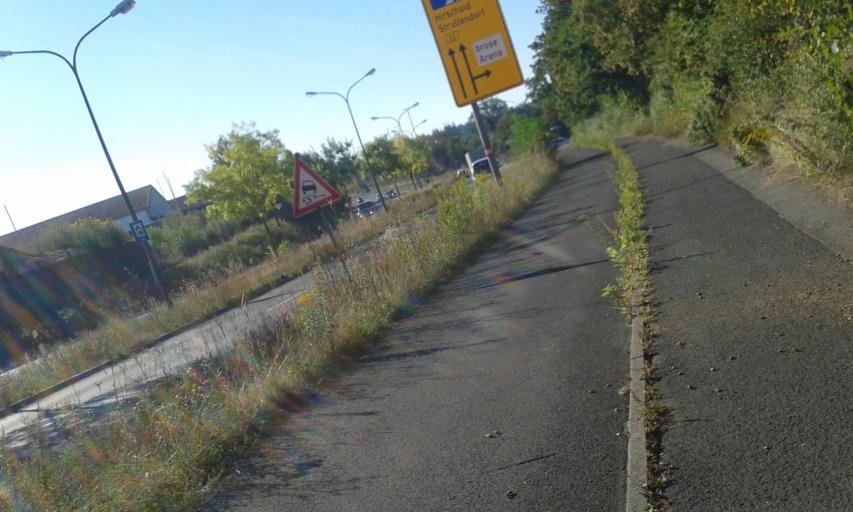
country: DE
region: Bavaria
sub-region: Upper Franconia
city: Bamberg
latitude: 49.8816
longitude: 10.9228
